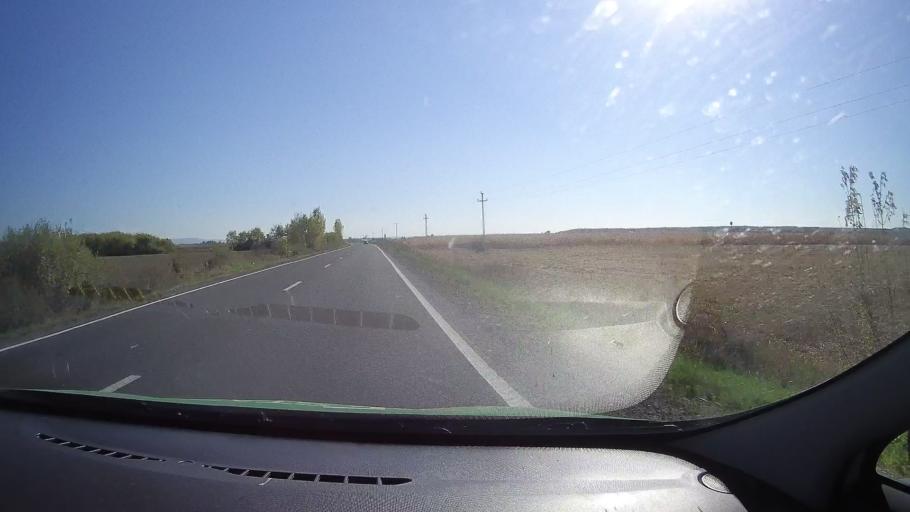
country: RO
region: Satu Mare
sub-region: Oras Ardud
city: Madaras
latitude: 47.6598
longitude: 22.8741
